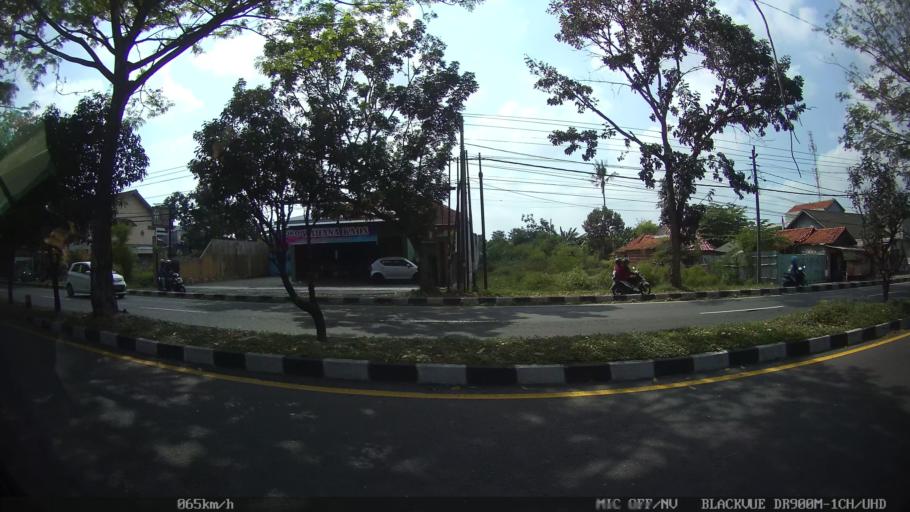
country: ID
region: Daerah Istimewa Yogyakarta
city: Gamping Lor
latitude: -7.7966
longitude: 110.3301
